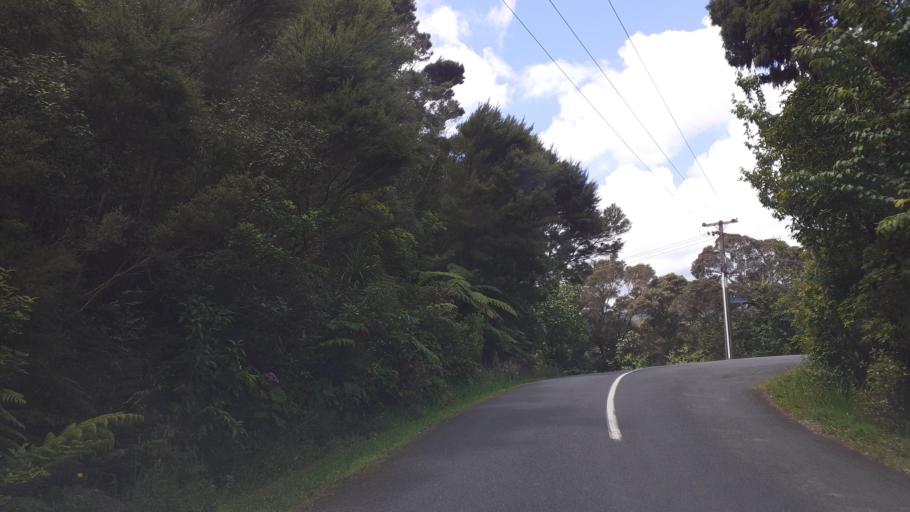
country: NZ
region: Northland
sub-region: Far North District
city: Paihia
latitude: -35.3116
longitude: 174.1135
